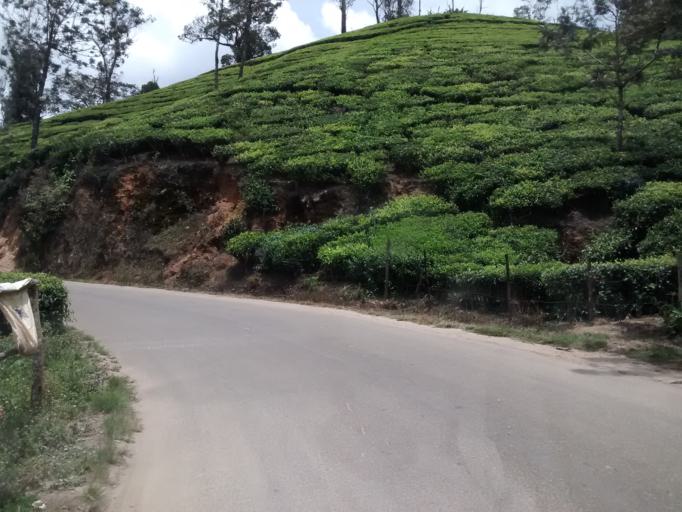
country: IN
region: Tamil Nadu
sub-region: Theni
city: Bodinayakkanur
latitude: 10.1286
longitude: 77.2350
